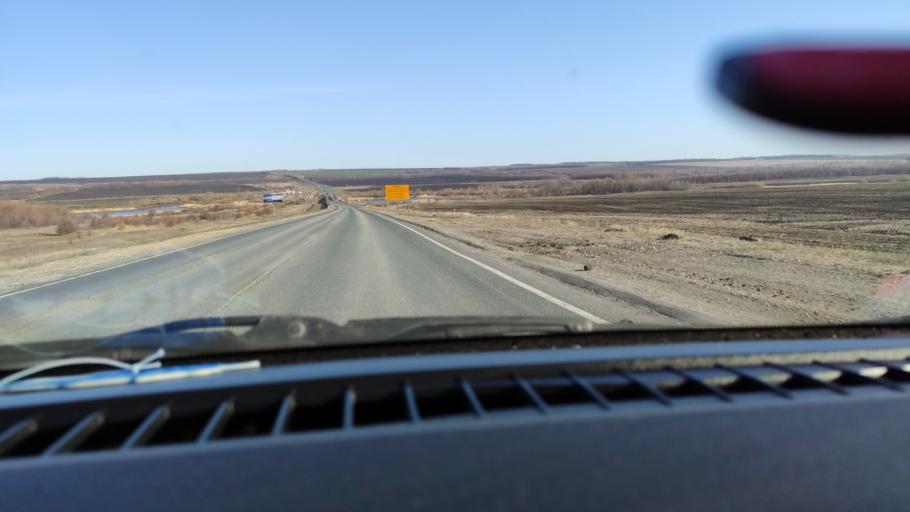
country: RU
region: Saratov
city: Dukhovnitskoye
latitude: 52.7307
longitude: 48.2584
